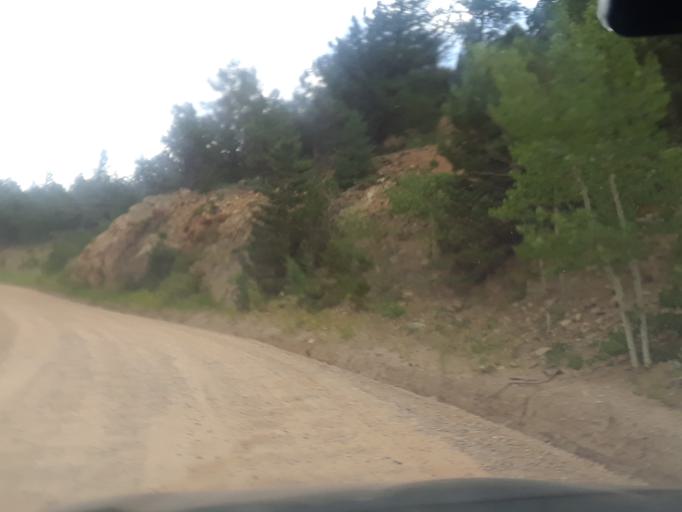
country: US
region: Colorado
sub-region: Boulder County
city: Boulder
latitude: 40.0652
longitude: -105.4057
